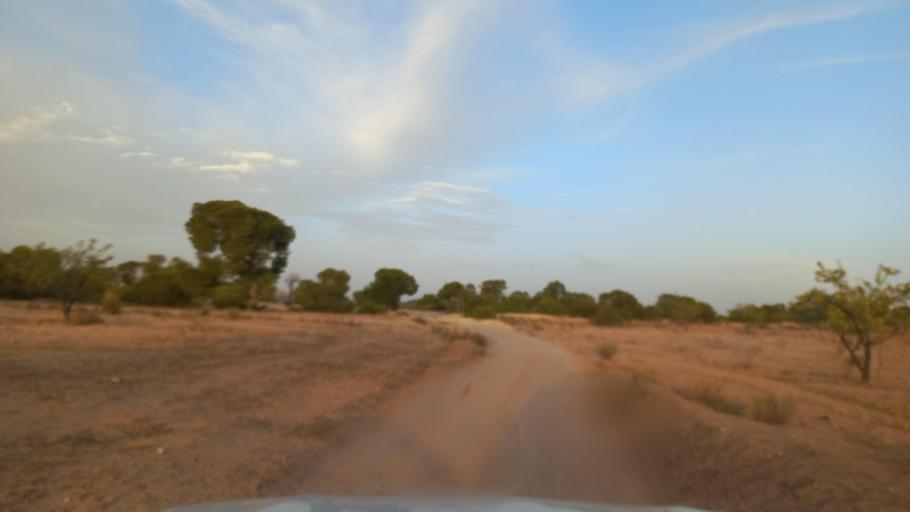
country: TN
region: Al Qasrayn
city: Sbiba
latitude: 35.4237
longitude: 8.9124
